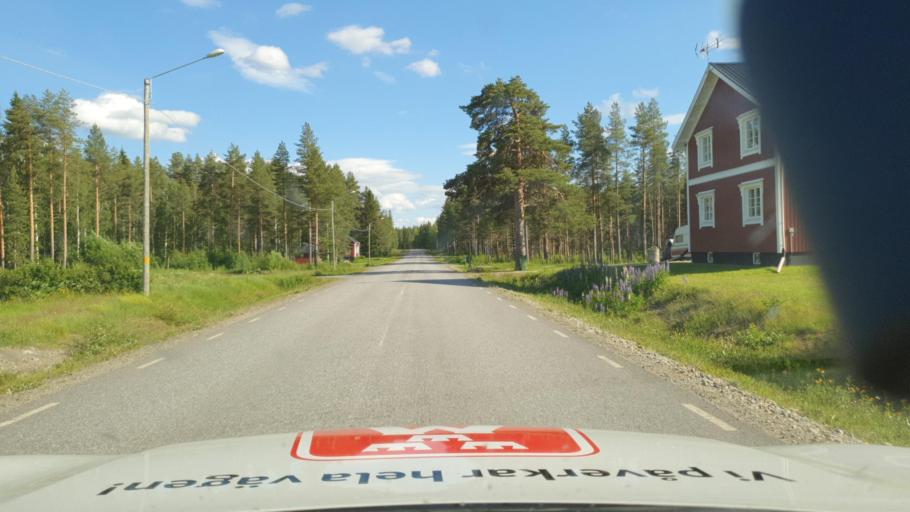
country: SE
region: Vaesterbotten
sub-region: Skelleftea Kommun
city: Langsele
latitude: 64.8007
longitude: 20.0096
